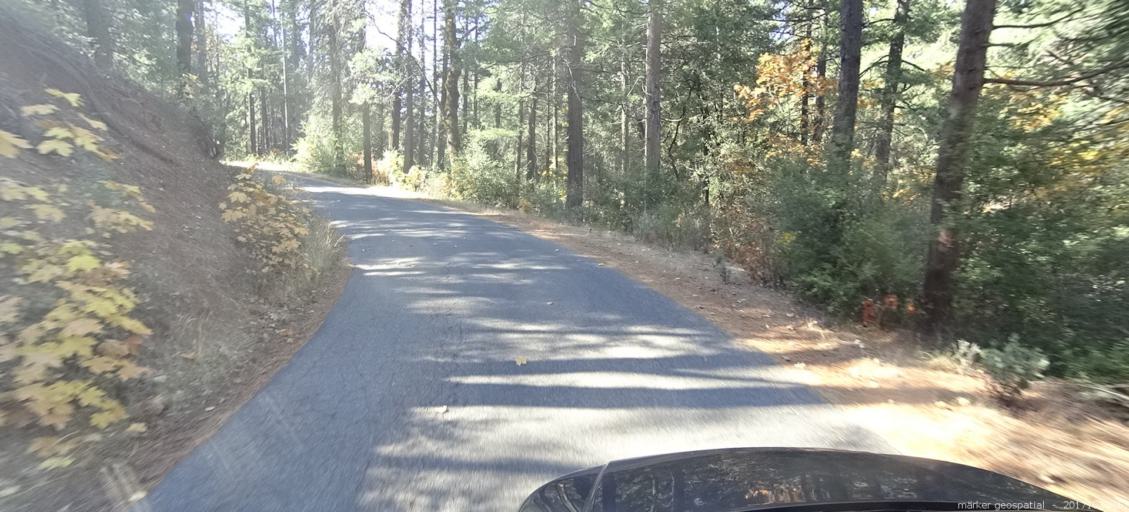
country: US
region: California
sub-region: Shasta County
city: Shingletown
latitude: 40.6067
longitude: -121.8548
